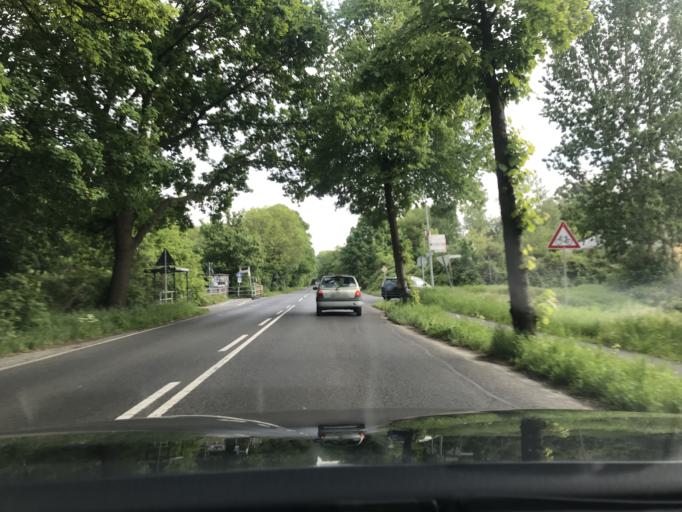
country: DE
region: North Rhine-Westphalia
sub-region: Regierungsbezirk Dusseldorf
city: Korschenbroich
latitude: 51.2392
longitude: 6.4840
